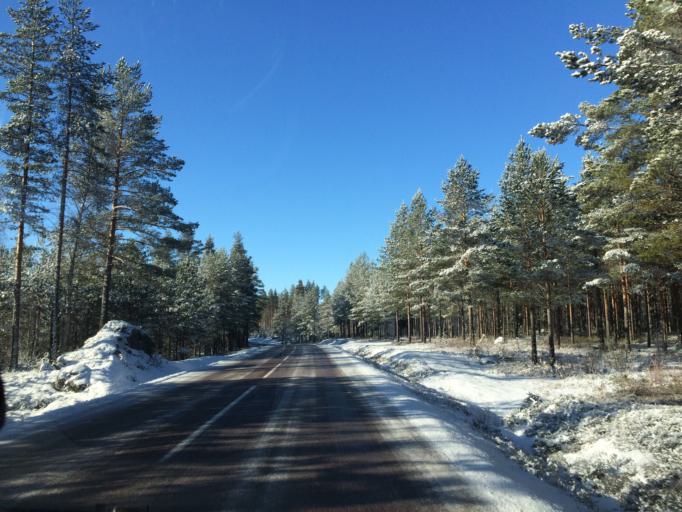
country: SE
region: Dalarna
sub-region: Vansbro Kommun
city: Vansbro
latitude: 60.7290
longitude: 14.1140
